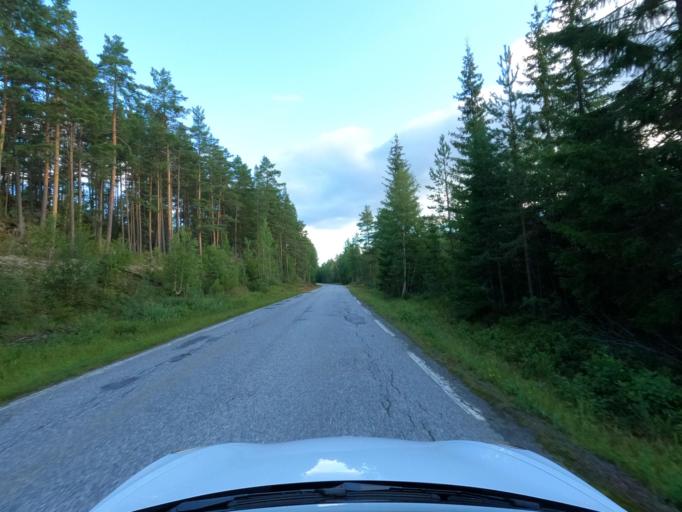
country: NO
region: Telemark
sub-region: Hjartdal
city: Sauland
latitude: 59.8070
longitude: 9.0842
